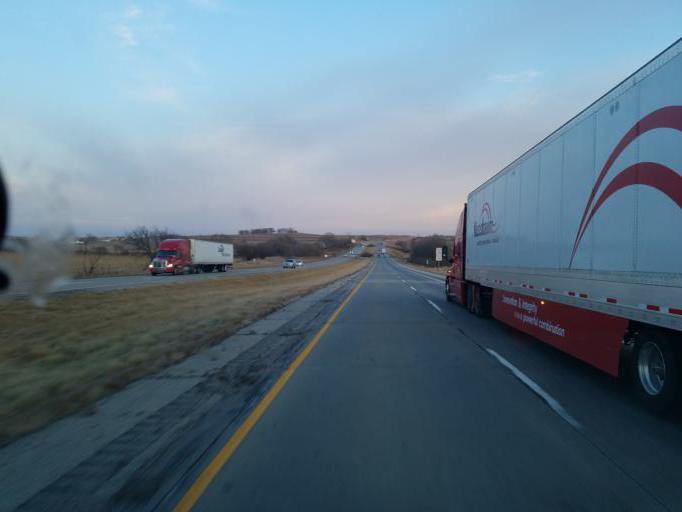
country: US
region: Iowa
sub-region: Pottawattamie County
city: Avoca
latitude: 41.4990
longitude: -95.5356
